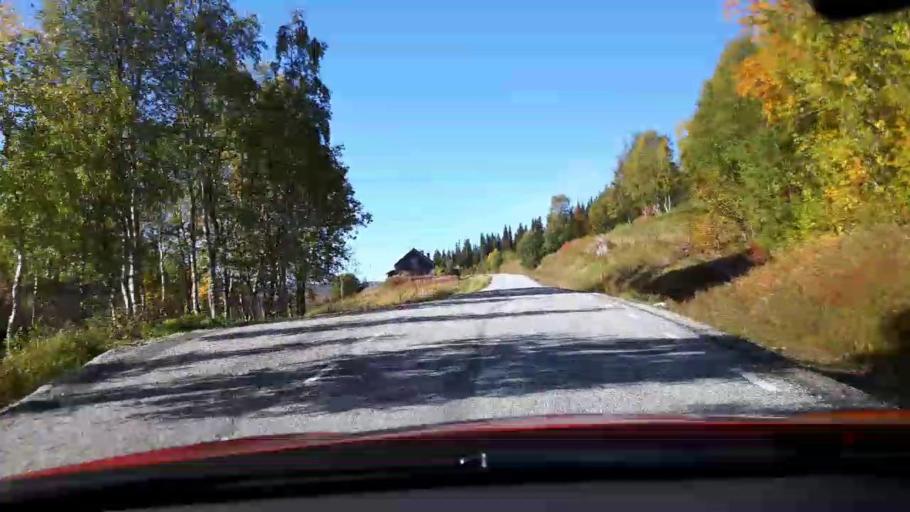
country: NO
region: Nord-Trondelag
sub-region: Royrvik
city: Royrvik
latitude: 64.8764
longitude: 14.2313
